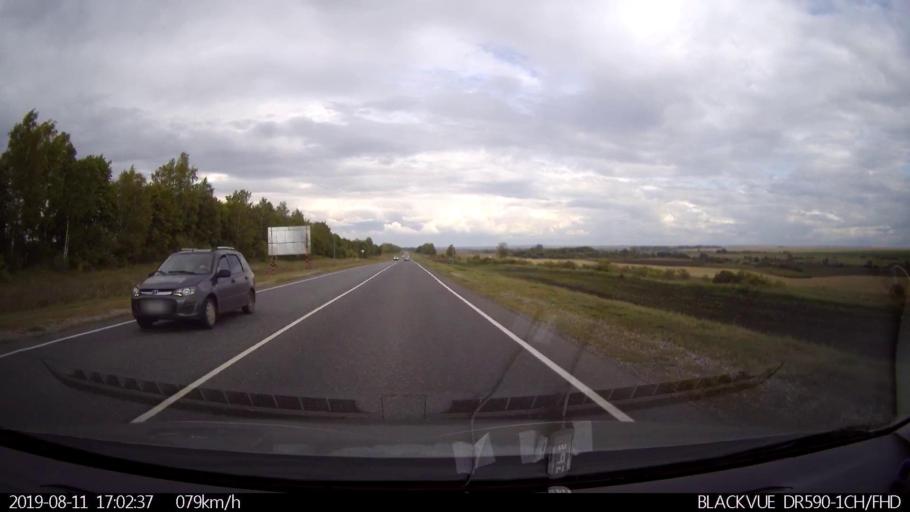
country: RU
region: Ulyanovsk
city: Mayna
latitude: 54.3055
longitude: 47.7191
